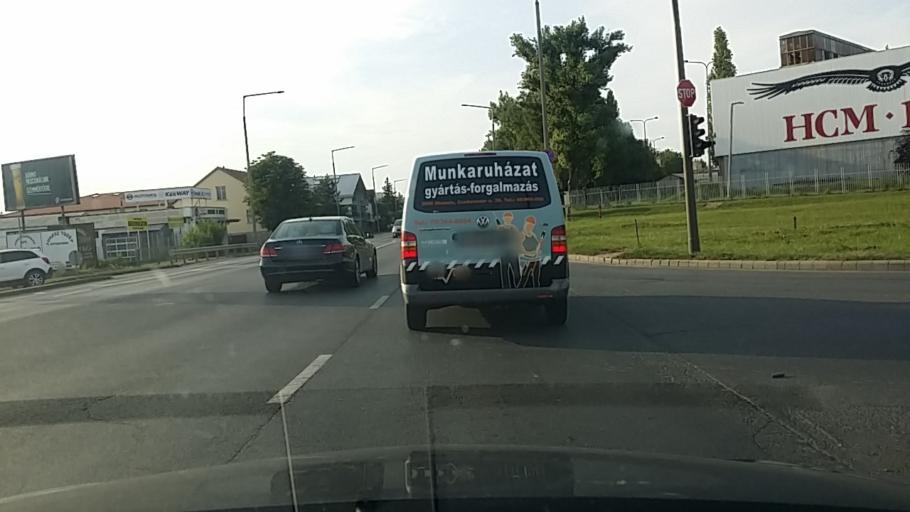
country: HU
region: Borsod-Abauj-Zemplen
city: Miskolc
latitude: 48.0613
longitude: 20.7951
